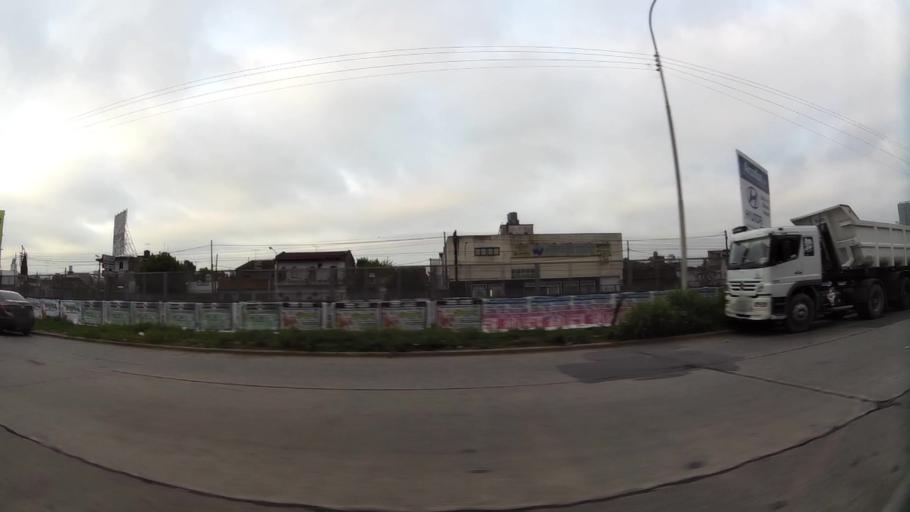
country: AR
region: Buenos Aires
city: San Justo
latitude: -34.6400
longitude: -58.5458
